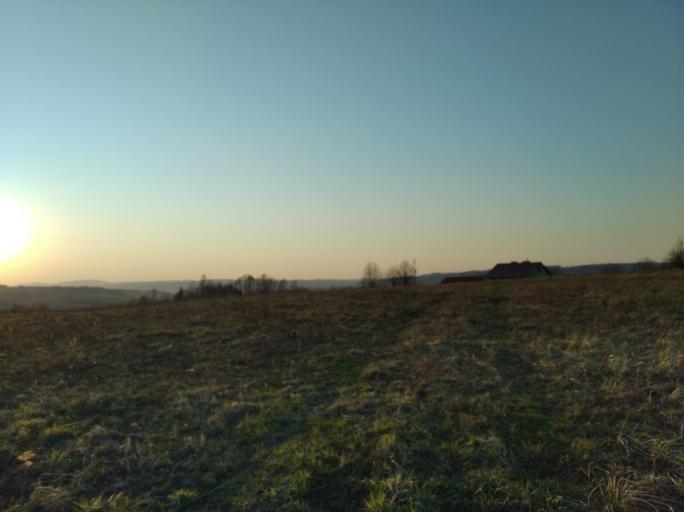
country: PL
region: Subcarpathian Voivodeship
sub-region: Powiat strzyzowski
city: Strzyzow
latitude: 49.8539
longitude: 21.8142
